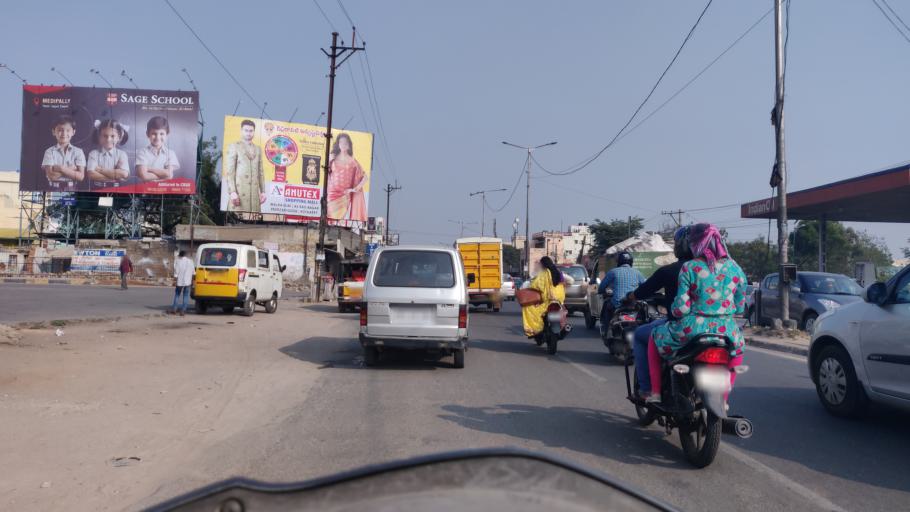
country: IN
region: Telangana
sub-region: Rangareddi
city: Uppal Kalan
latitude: 17.4015
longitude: 78.5688
